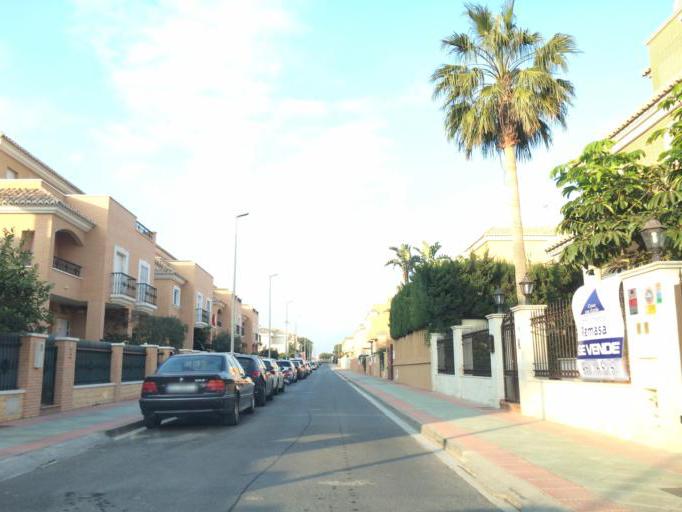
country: ES
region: Andalusia
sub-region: Provincia de Almeria
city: Almeria
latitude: 36.8219
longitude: -2.4381
